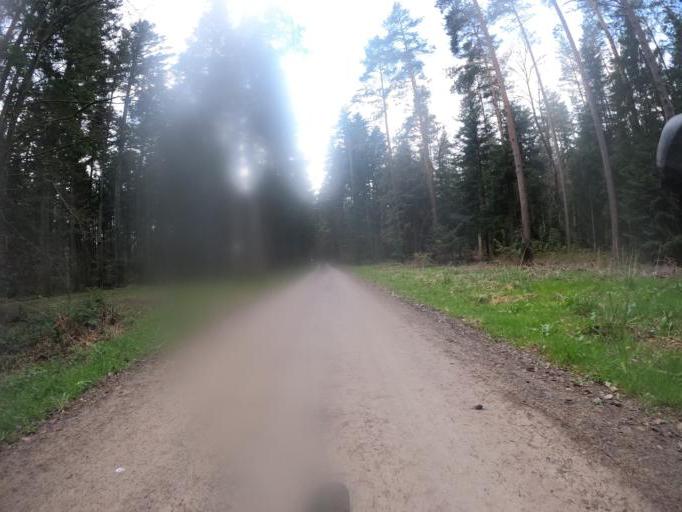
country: DE
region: Baden-Wuerttemberg
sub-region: Karlsruhe Region
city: Oberreichenbach
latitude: 48.7154
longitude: 8.6504
